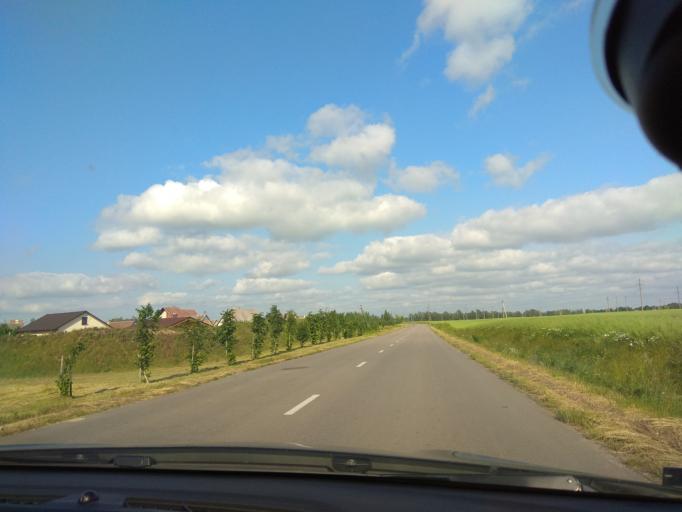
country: LT
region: Siauliu apskritis
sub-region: Joniskis
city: Joniskis
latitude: 56.2282
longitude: 23.6203
